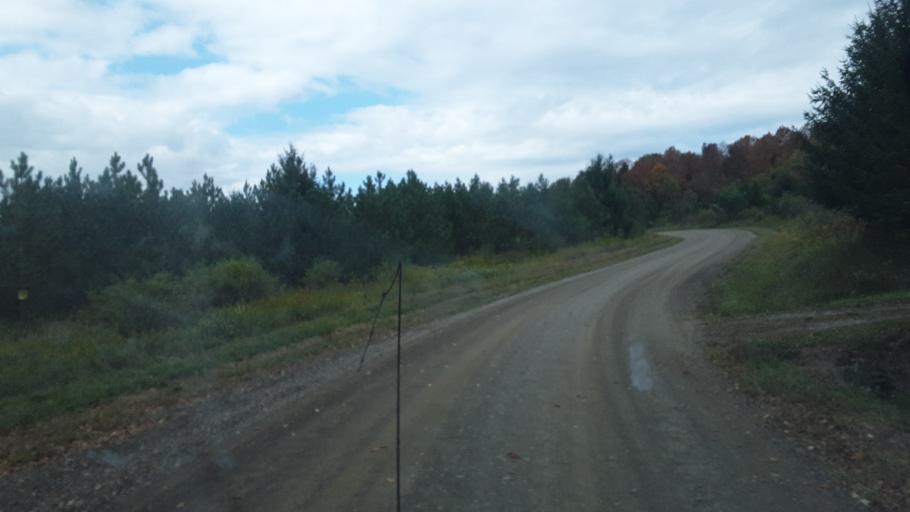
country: US
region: New York
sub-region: Allegany County
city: Alfred
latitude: 42.3834
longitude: -77.8609
